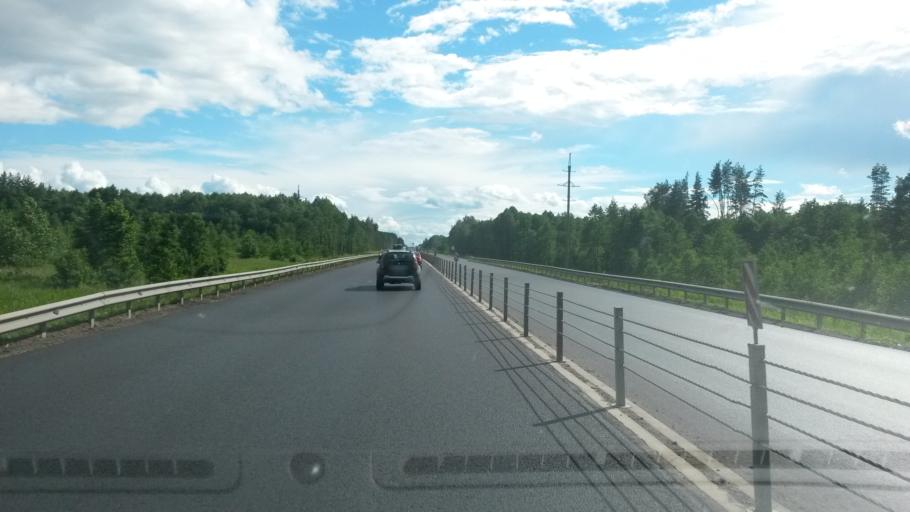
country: RU
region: Jaroslavl
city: Semibratovo
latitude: 57.2570
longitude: 39.4871
